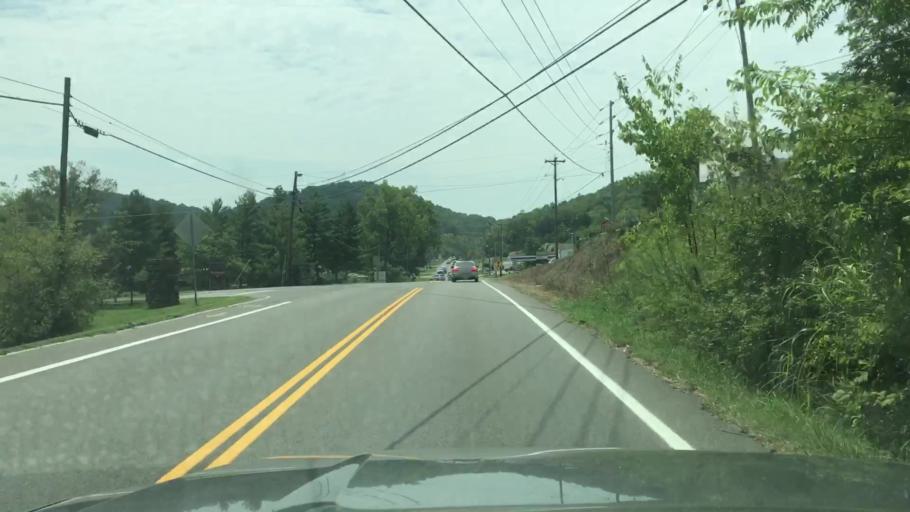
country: US
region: Tennessee
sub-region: Williamson County
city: Franklin
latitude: 35.9996
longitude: -86.8857
